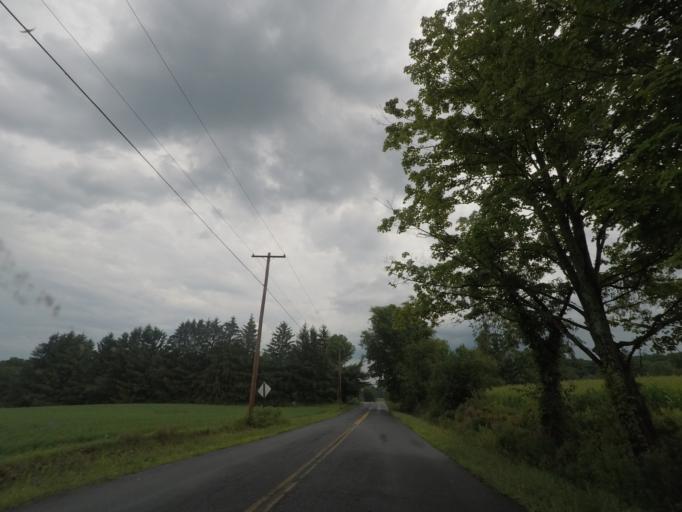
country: US
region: New York
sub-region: Rensselaer County
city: Poestenkill
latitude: 42.7255
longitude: -73.5899
